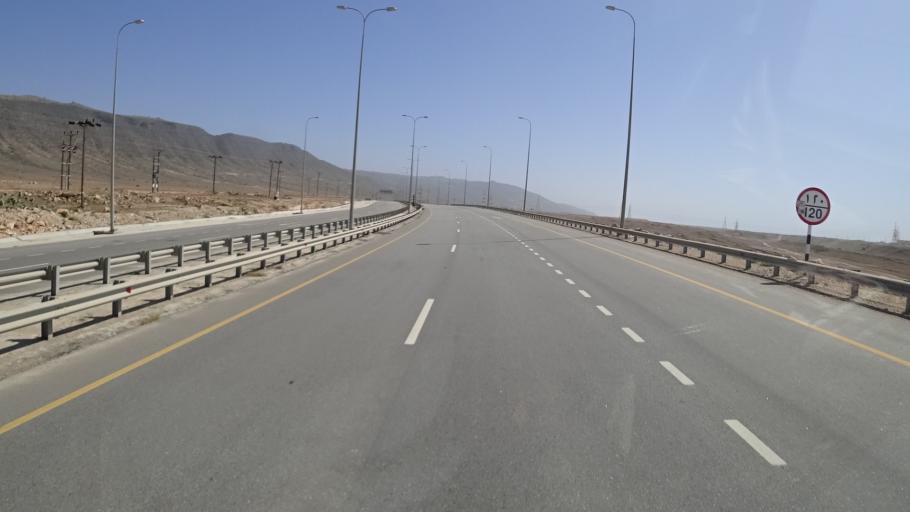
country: OM
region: Zufar
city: Salalah
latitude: 17.0478
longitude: 54.4812
